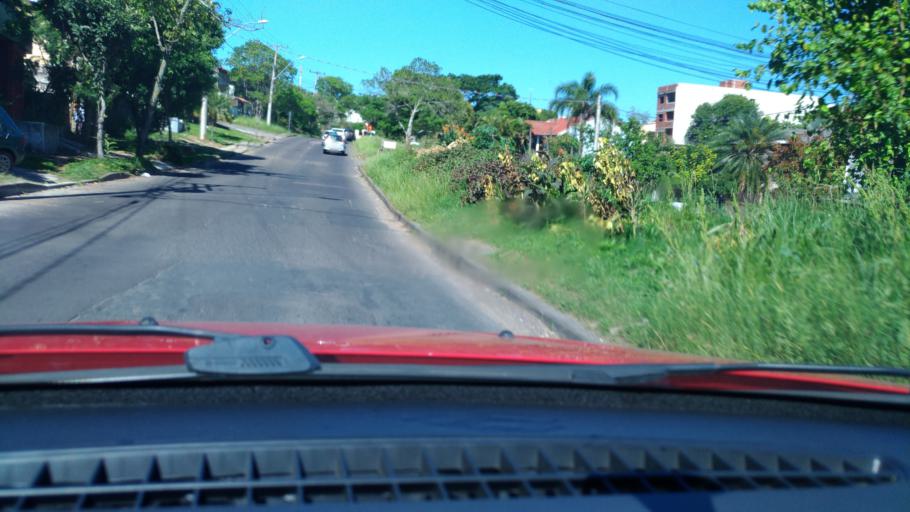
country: BR
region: Rio Grande do Sul
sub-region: Porto Alegre
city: Porto Alegre
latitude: -30.0331
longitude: -51.1484
